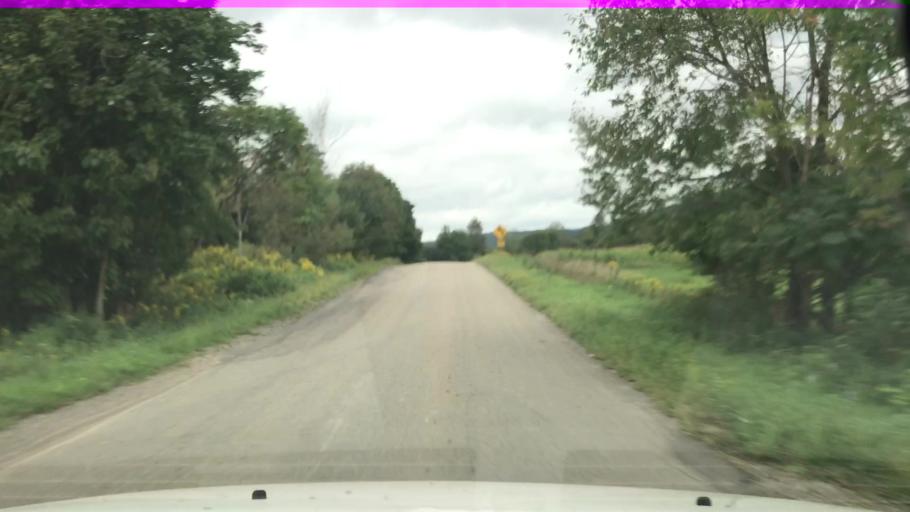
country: US
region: New York
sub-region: Cattaraugus County
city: Little Valley
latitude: 42.3169
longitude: -78.7221
